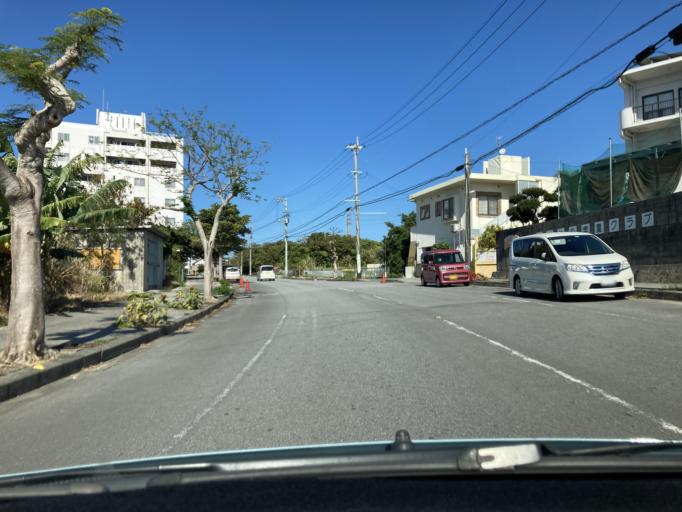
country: JP
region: Okinawa
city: Gushikawa
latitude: 26.3822
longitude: 127.8693
